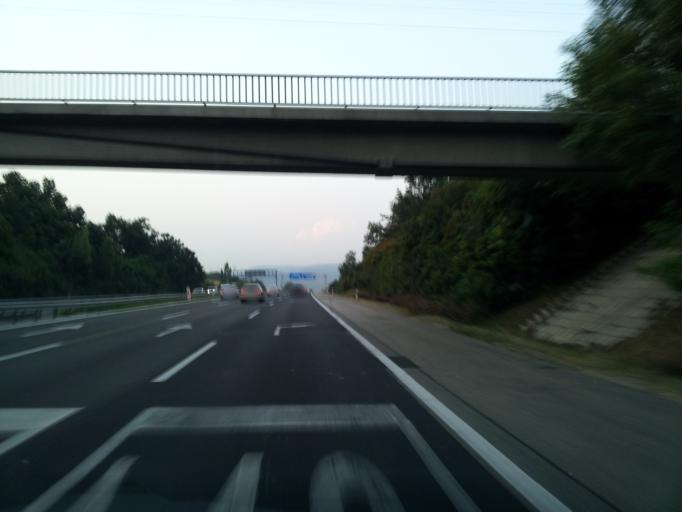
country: HU
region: Pest
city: Toeroekbalint
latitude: 47.4237
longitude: 18.8873
